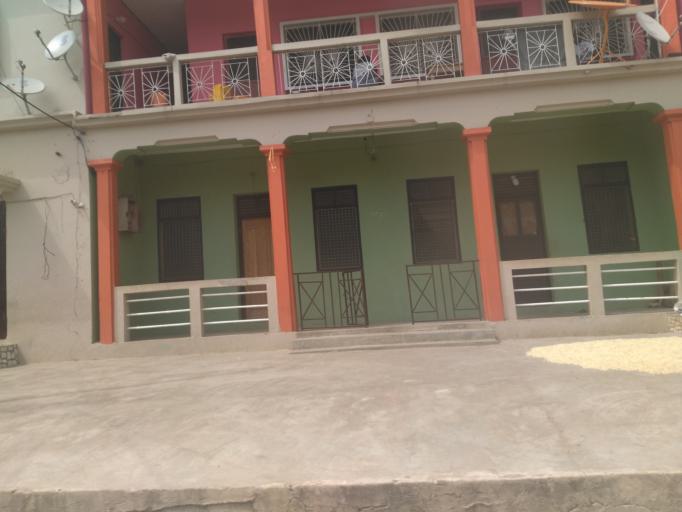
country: GH
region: Ashanti
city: Kumasi
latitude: 6.7063
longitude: -1.6206
